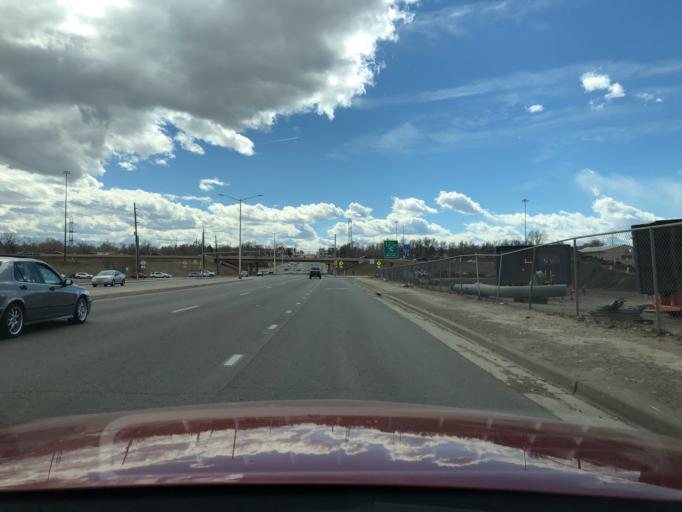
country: US
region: Colorado
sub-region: Adams County
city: Berkley
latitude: 39.8031
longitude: -105.0255
